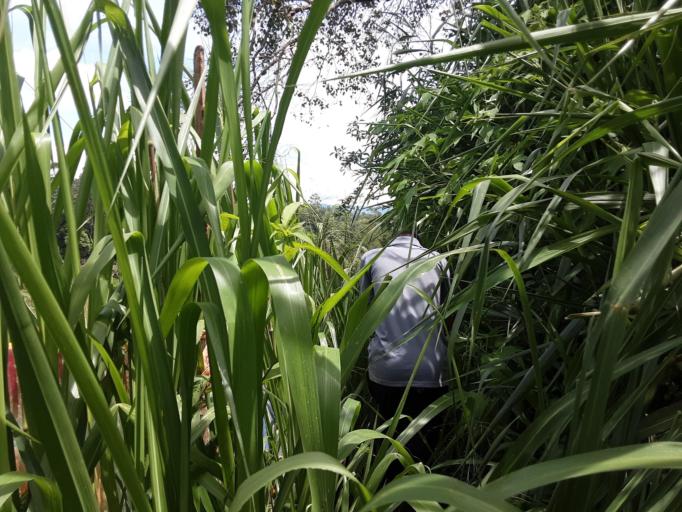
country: LK
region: Uva
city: Haputale
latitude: 6.8950
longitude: 80.9261
